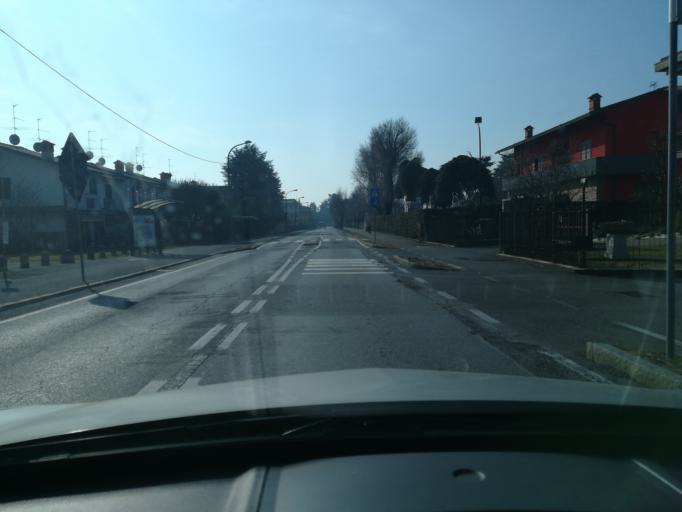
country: IT
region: Lombardy
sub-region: Provincia di Bergamo
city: Stezzano
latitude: 45.6561
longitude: 9.6557
